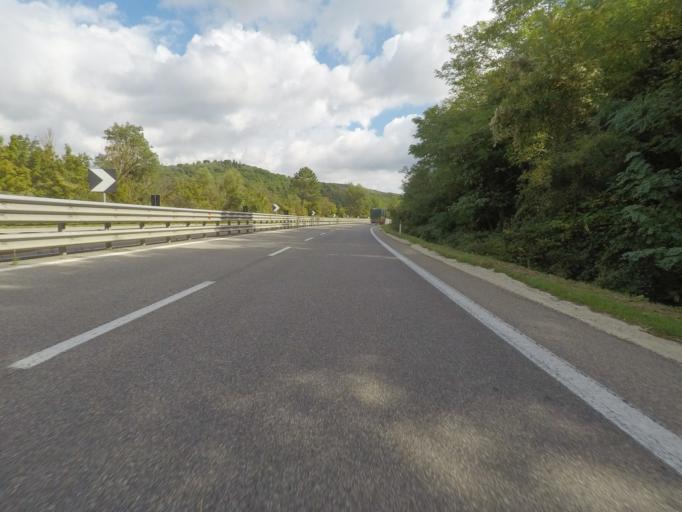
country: IT
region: Tuscany
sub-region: Province of Arezzo
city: Lucignano
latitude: 43.2554
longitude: 11.6891
